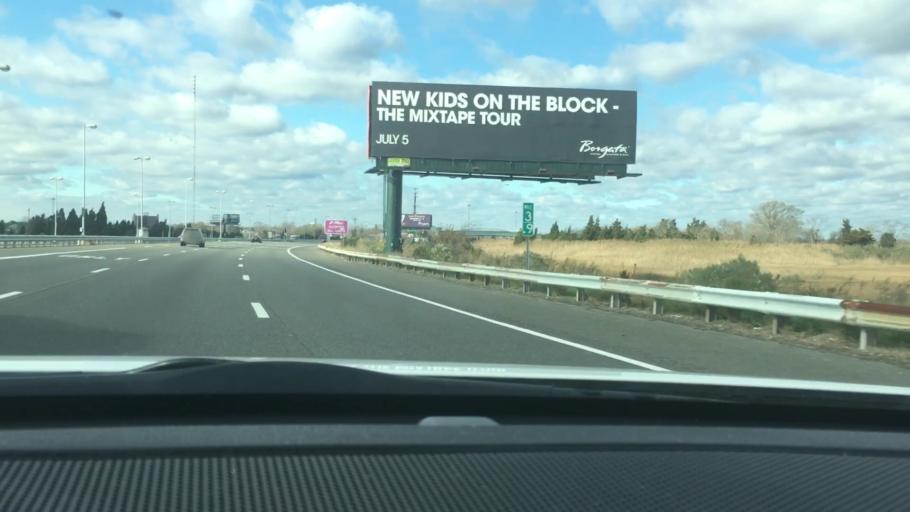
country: US
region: New Jersey
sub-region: Atlantic County
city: Pleasantville
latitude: 39.3866
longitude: -74.5054
